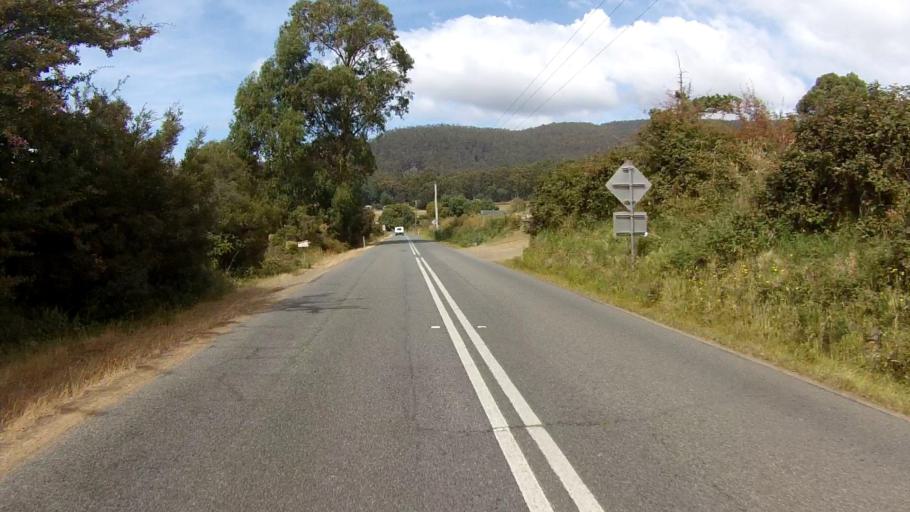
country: AU
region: Tasmania
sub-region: Kingborough
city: Kettering
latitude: -43.2121
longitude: 147.2561
